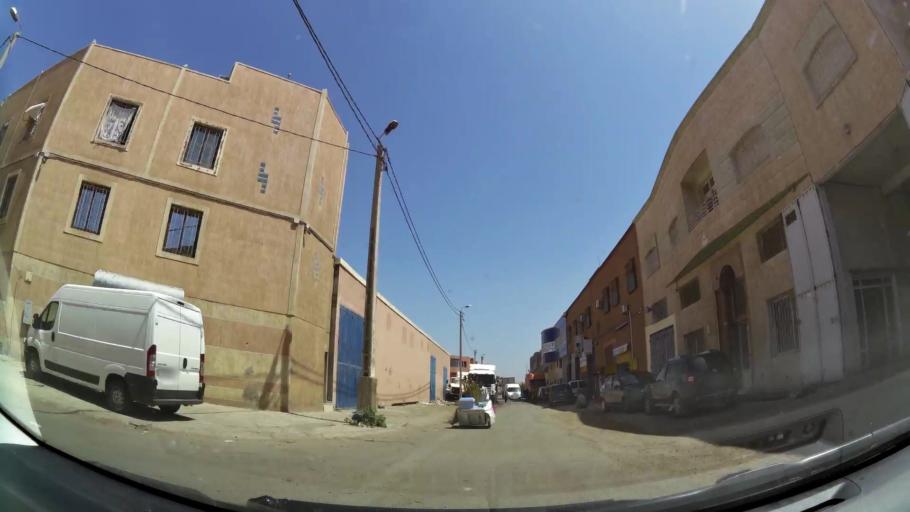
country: MA
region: Souss-Massa-Draa
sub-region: Inezgane-Ait Mellou
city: Inezgane
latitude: 30.3382
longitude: -9.4880
